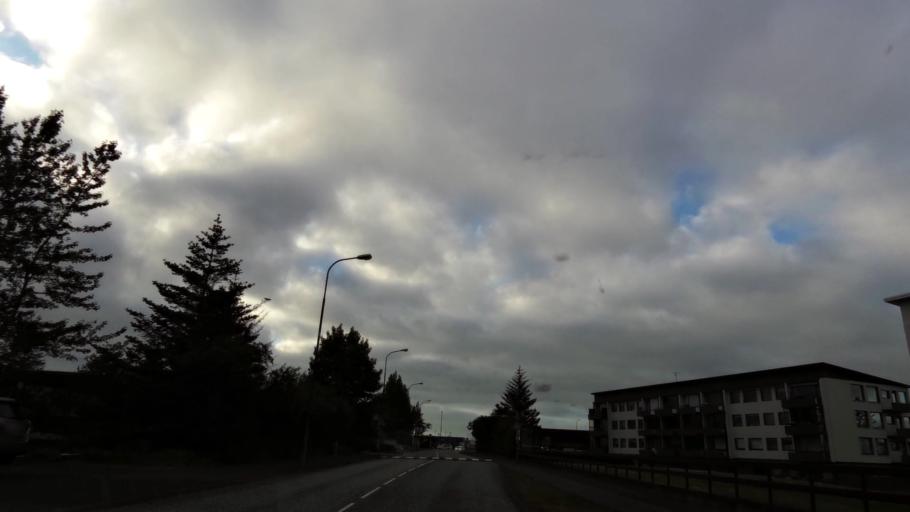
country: IS
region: Capital Region
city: Hafnarfjoerdur
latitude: 64.0745
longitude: -21.9422
